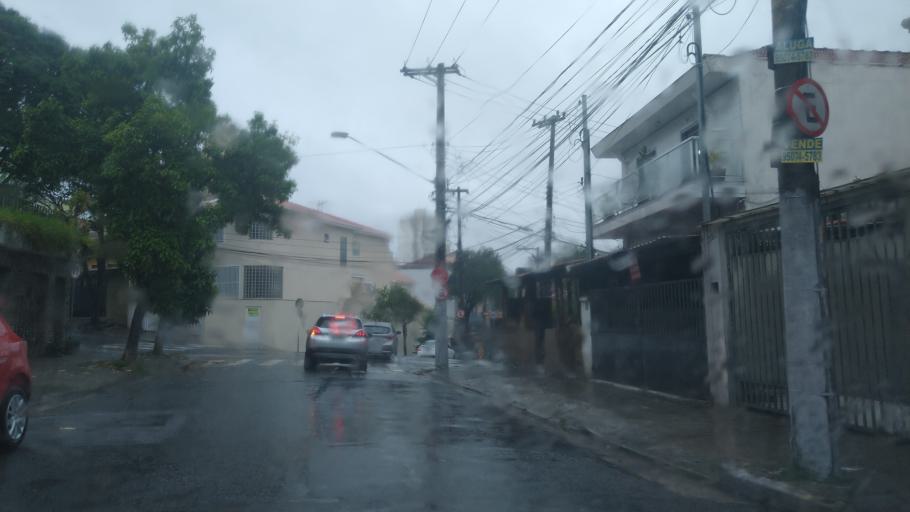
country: BR
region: Sao Paulo
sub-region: Sao Paulo
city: Sao Paulo
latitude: -23.4898
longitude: -46.6204
